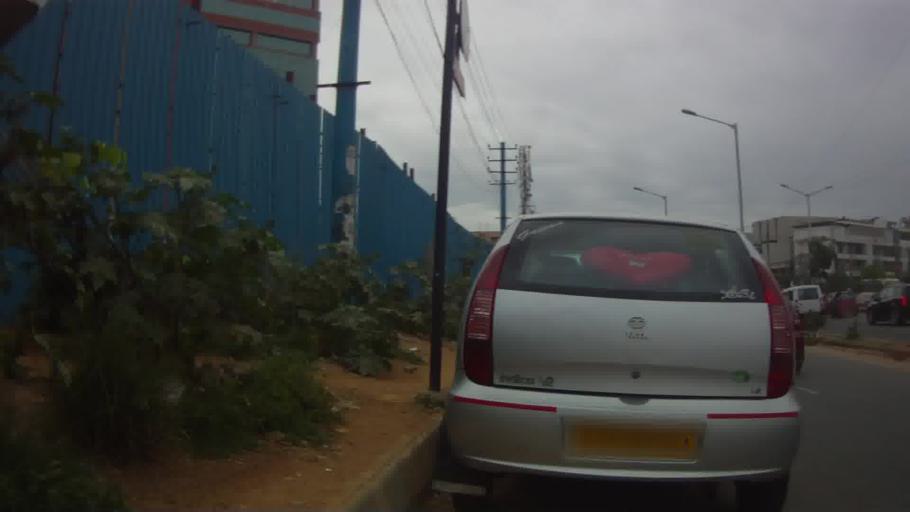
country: IN
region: Karnataka
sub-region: Bangalore Urban
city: Bangalore
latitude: 12.9804
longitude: 77.6944
